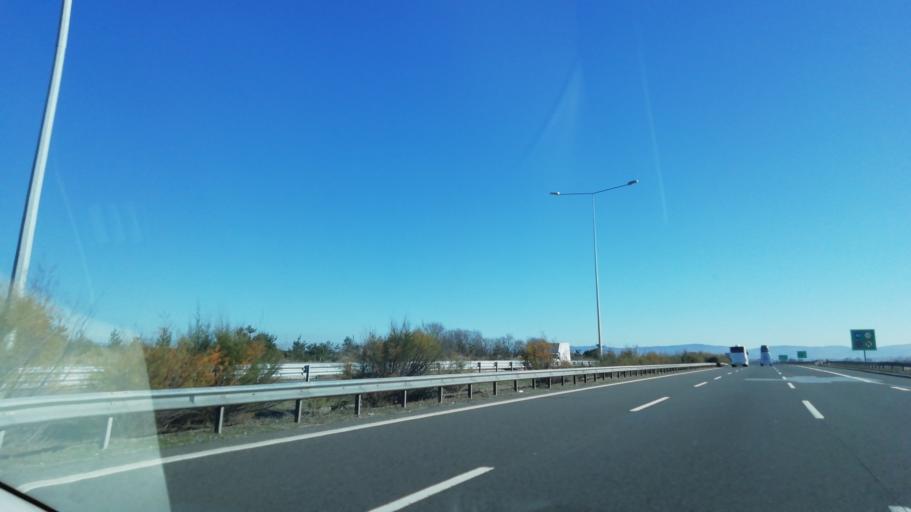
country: TR
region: Bolu
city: Dortdivan
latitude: 40.7412
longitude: 32.1280
